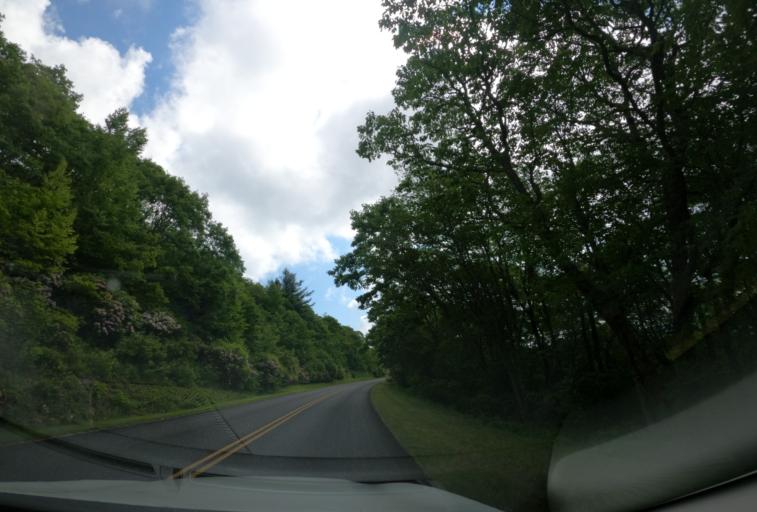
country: US
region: North Carolina
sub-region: Haywood County
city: Hazelwood
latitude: 35.4122
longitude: -83.0426
